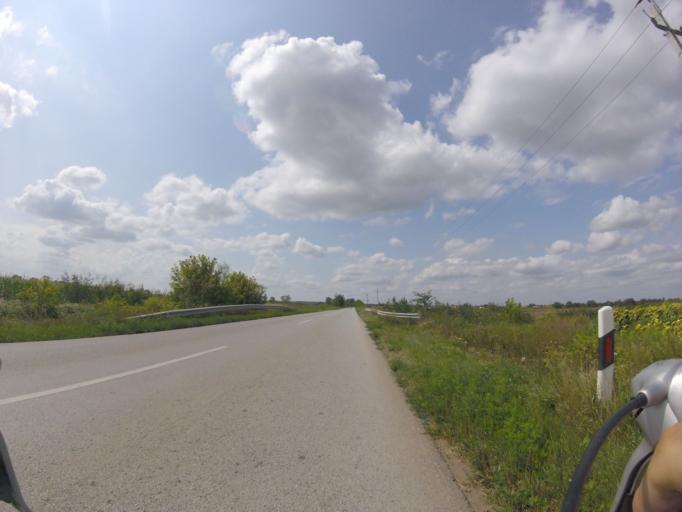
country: HU
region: Szabolcs-Szatmar-Bereg
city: Kemecse
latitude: 48.0668
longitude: 21.8205
